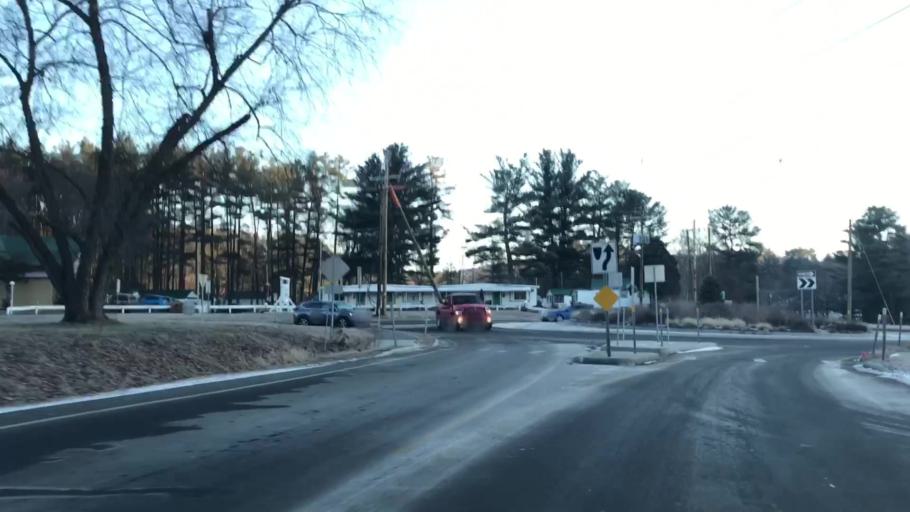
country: US
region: New Hampshire
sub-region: Cheshire County
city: Keene
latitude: 42.9080
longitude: -72.2598
